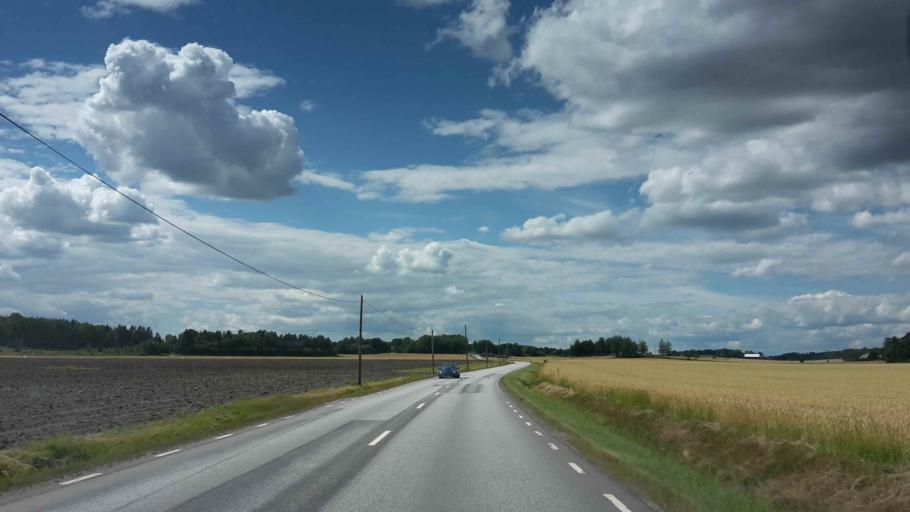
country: SE
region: OEstergoetland
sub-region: Soderkopings Kommun
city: Soederkoeping
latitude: 58.5262
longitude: 16.4341
